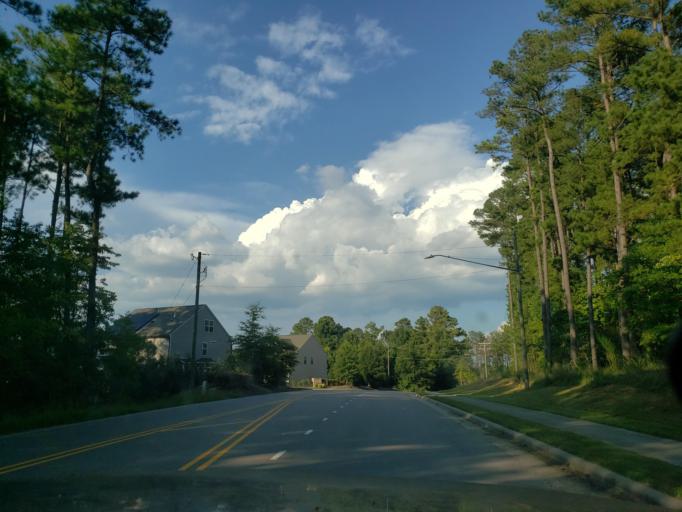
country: US
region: North Carolina
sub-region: Durham County
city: Durham
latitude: 35.9421
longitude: -78.9246
